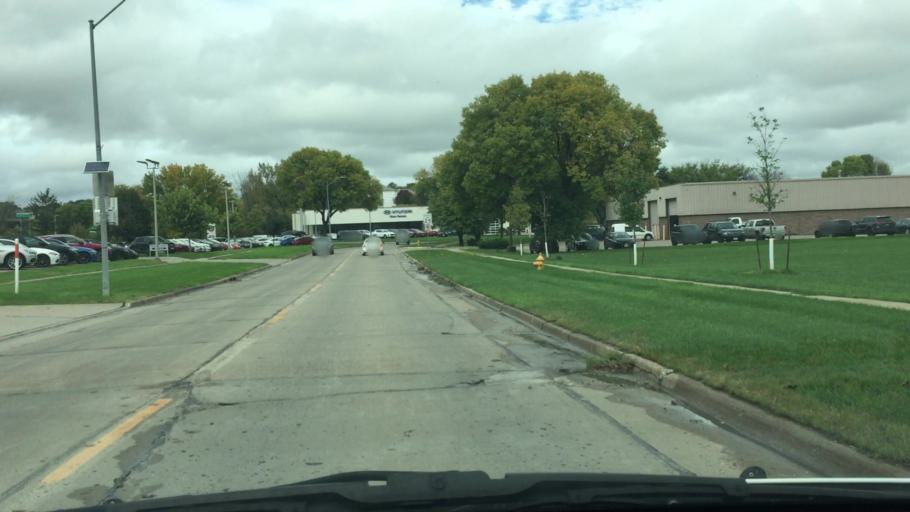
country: US
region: Iowa
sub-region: Polk County
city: Clive
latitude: 41.6117
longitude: -93.7749
